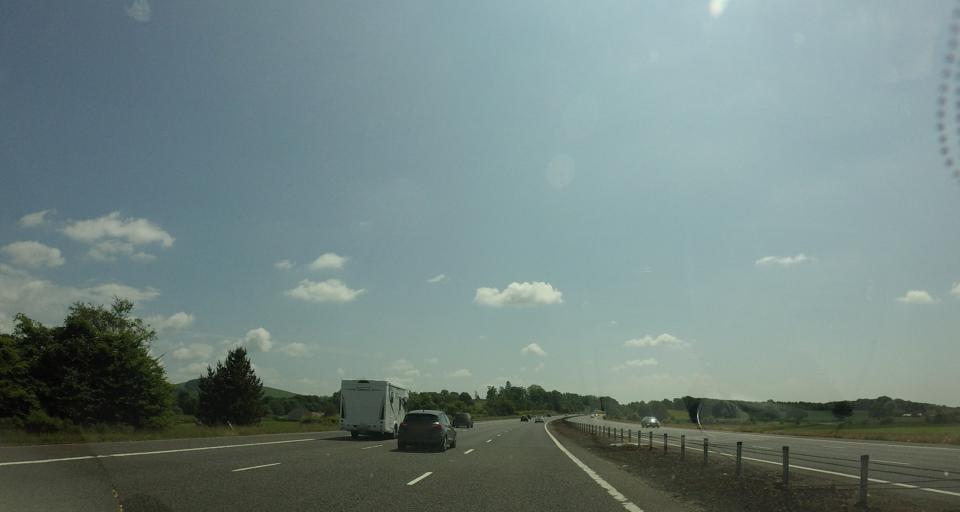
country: GB
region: Scotland
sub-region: Dumfries and Galloway
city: Lockerbie
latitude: 55.1437
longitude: -3.3758
